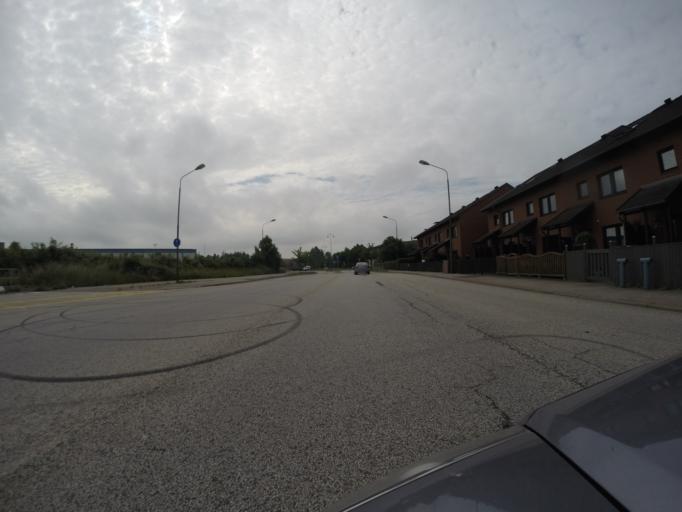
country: SE
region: Skane
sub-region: Burlovs Kommun
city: Arloev
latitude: 55.6359
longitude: 13.0660
